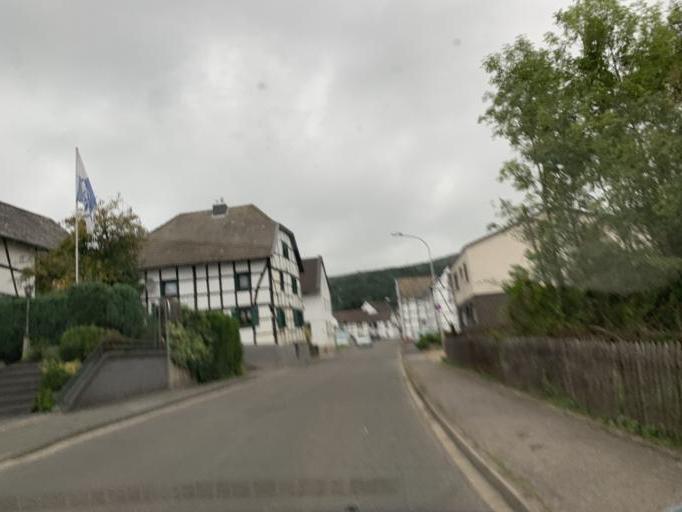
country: DE
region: North Rhine-Westphalia
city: Heimbach
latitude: 50.6368
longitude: 6.4598
